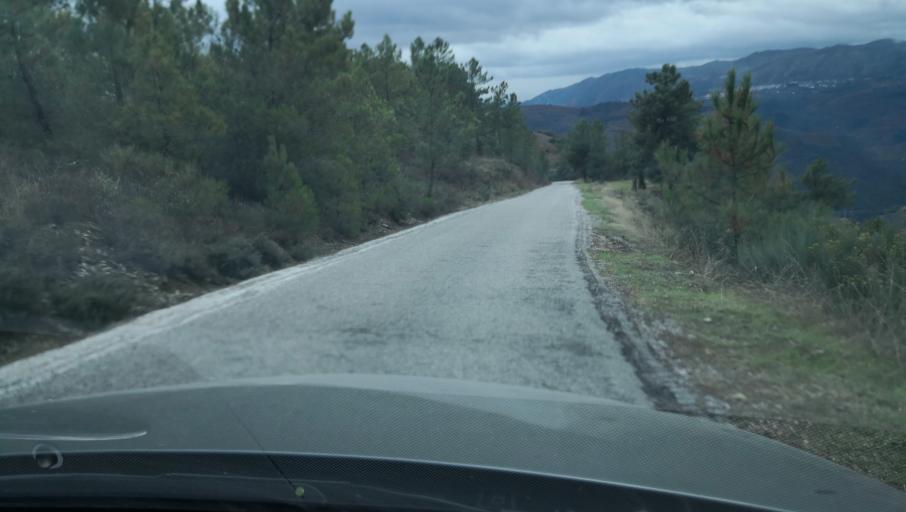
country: PT
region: Vila Real
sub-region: Sabrosa
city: Vilela
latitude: 41.1860
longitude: -7.5736
